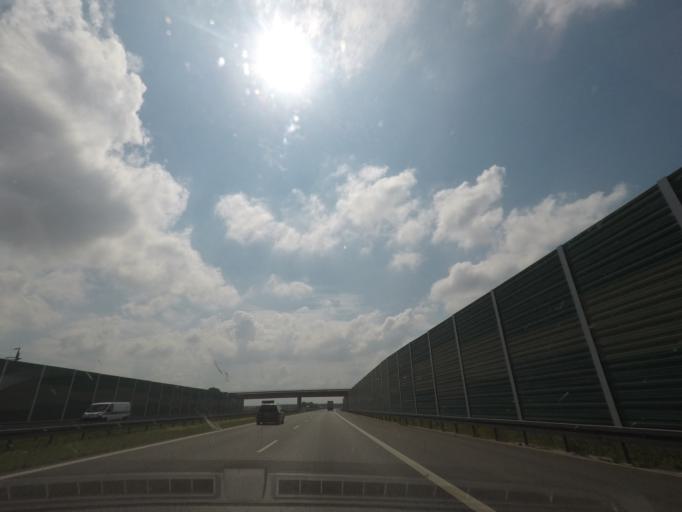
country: PL
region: Lodz Voivodeship
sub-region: Powiat kutnowski
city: Krzyzanow
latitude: 52.2141
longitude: 19.4774
